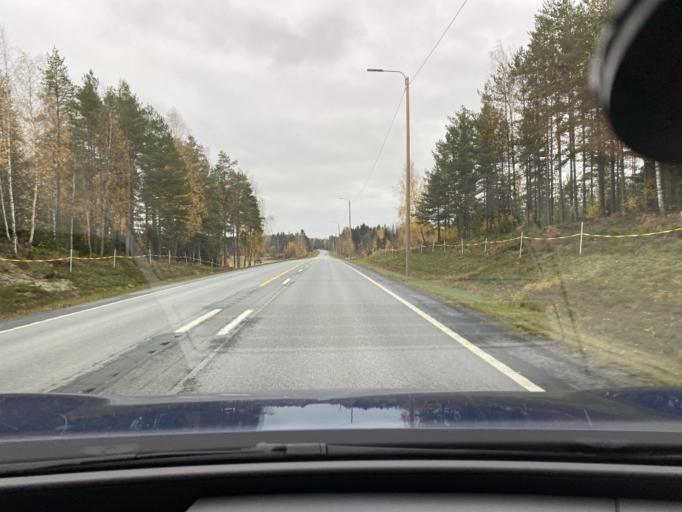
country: FI
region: Varsinais-Suomi
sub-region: Vakka-Suomi
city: Laitila
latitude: 60.9434
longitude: 21.6013
